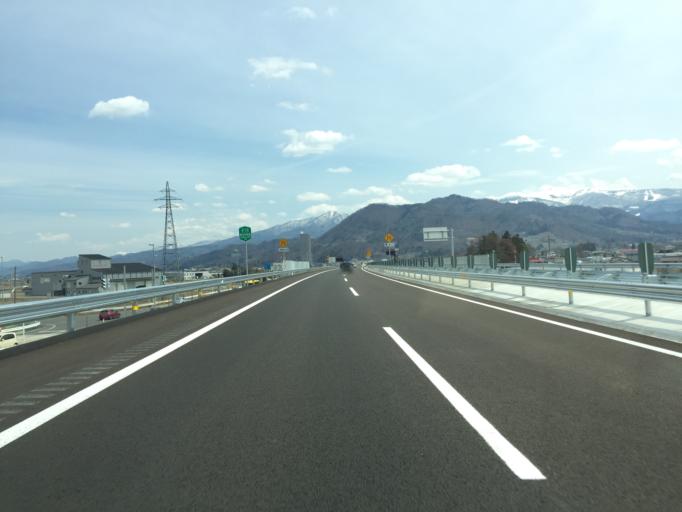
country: JP
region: Yamagata
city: Kaminoyama
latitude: 38.1279
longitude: 140.2584
